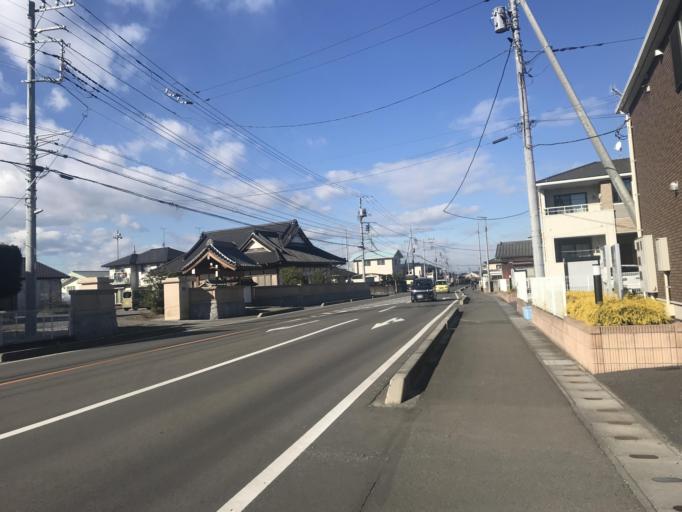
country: JP
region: Tochigi
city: Kaminokawa
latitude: 36.3763
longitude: 139.8785
